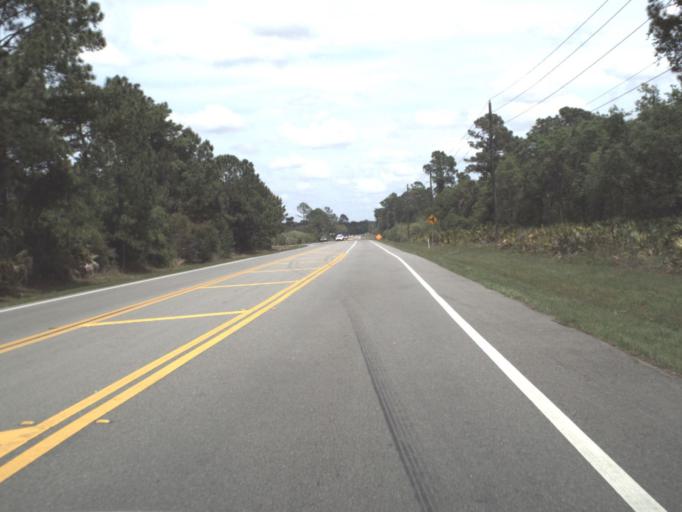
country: US
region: Florida
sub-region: Lake County
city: Lake Mack-Forest Hills
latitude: 28.9172
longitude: -81.4455
